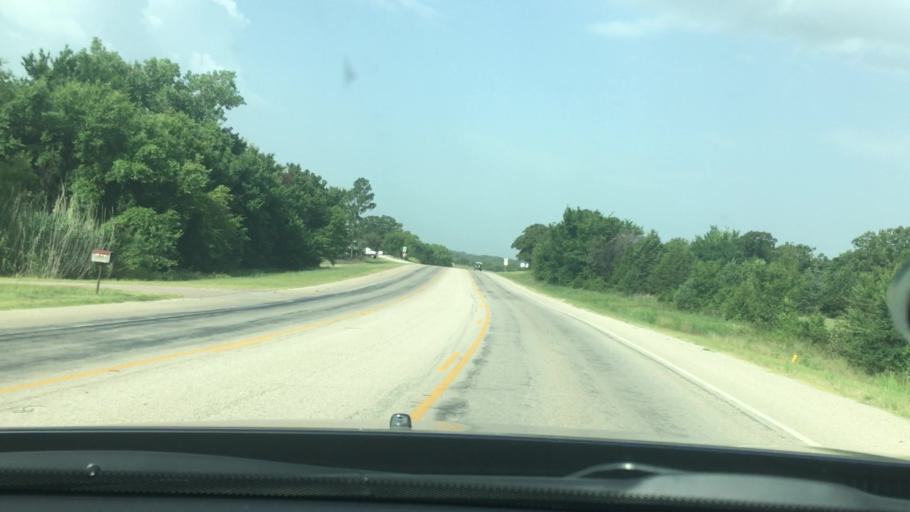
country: US
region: Oklahoma
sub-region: Pontotoc County
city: Ada
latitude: 34.7854
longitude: -96.7369
